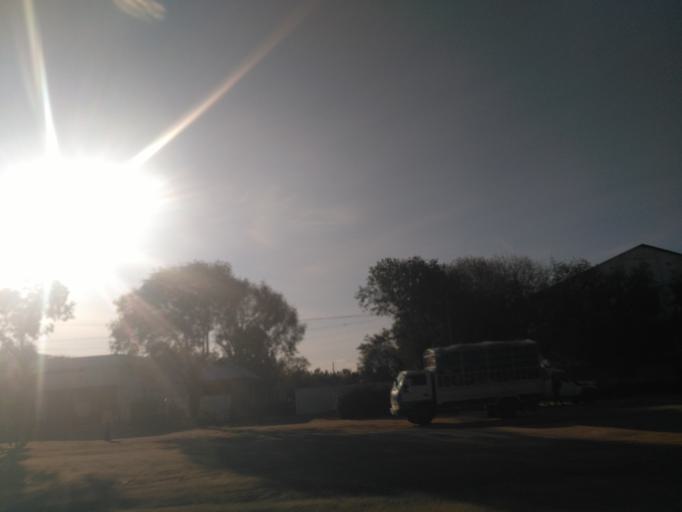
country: TZ
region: Dodoma
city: Dodoma
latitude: -6.1646
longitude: 35.7460
